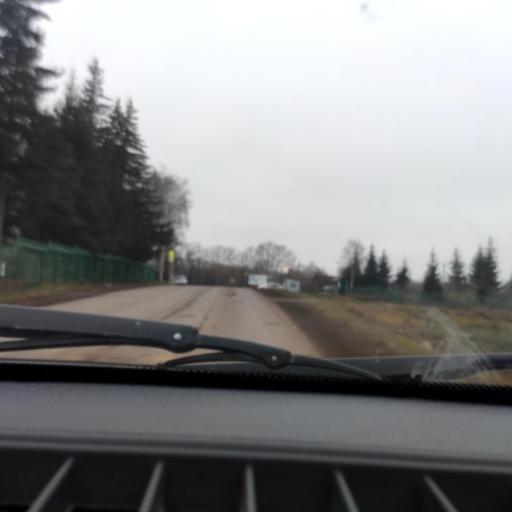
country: RU
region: Bashkortostan
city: Avdon
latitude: 54.6552
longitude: 55.7597
